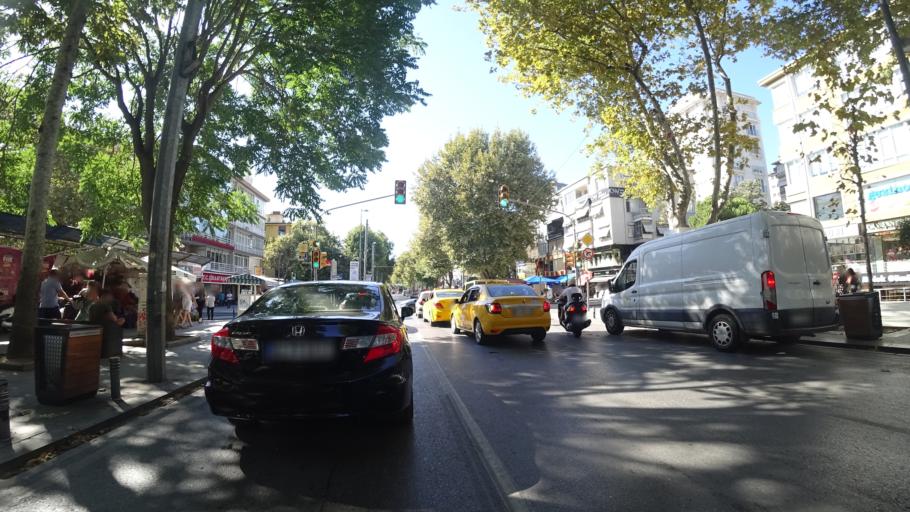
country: TR
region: Istanbul
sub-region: Atasehir
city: Atasehir
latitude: 40.9633
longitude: 29.0750
